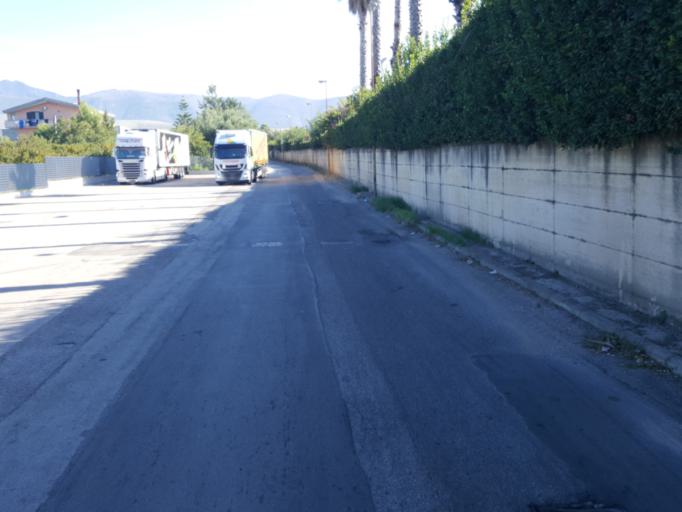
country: IT
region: Campania
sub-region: Provincia di Caserta
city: Pignataro Maggiore
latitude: 41.1614
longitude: 14.1623
